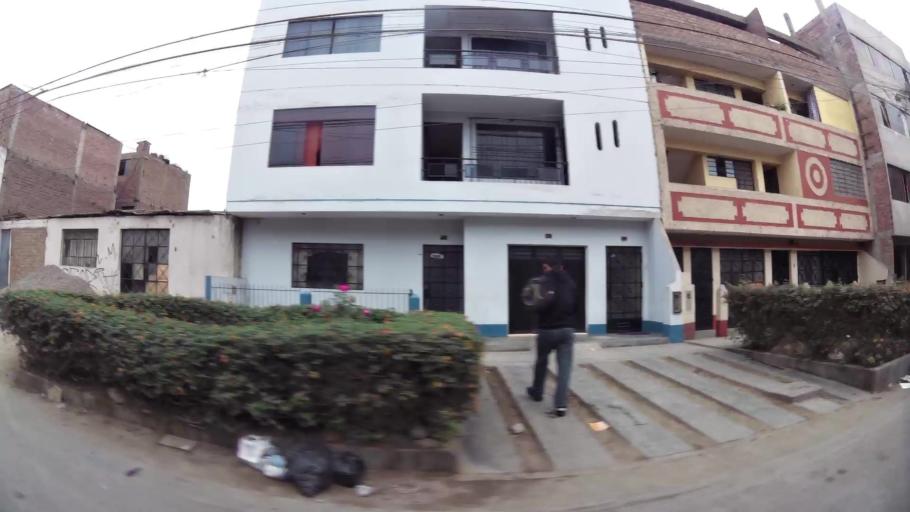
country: PE
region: Lima
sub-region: Lima
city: Independencia
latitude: -11.9932
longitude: -77.0067
